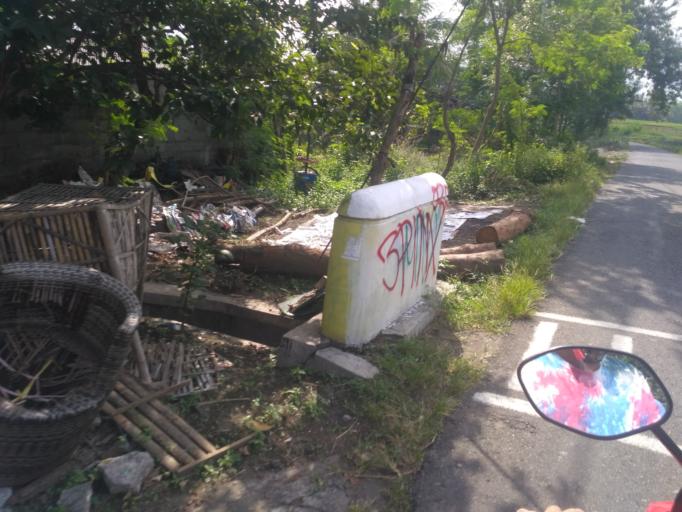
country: ID
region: Daerah Istimewa Yogyakarta
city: Godean
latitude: -7.7466
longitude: 110.3202
